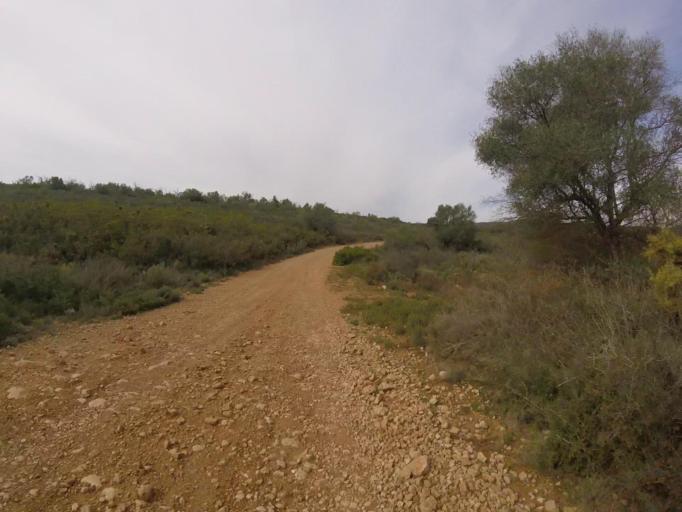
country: ES
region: Valencia
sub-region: Provincia de Castello
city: Torreblanca
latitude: 40.1963
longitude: 0.1318
